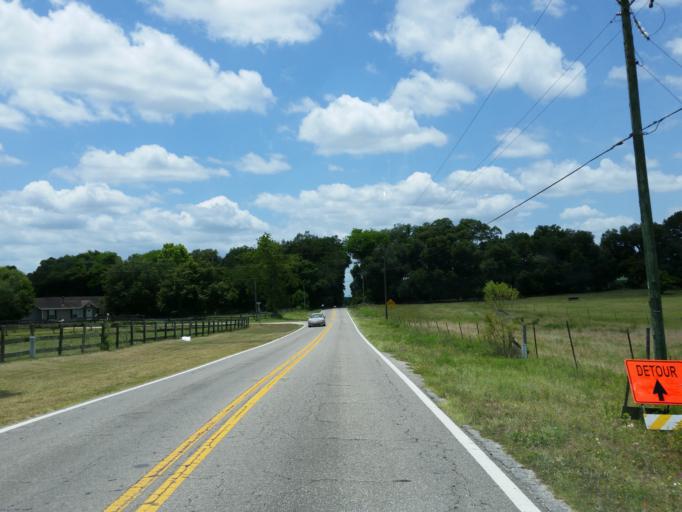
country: US
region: Florida
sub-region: Marion County
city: Belleview
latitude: 29.0114
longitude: -82.0554
